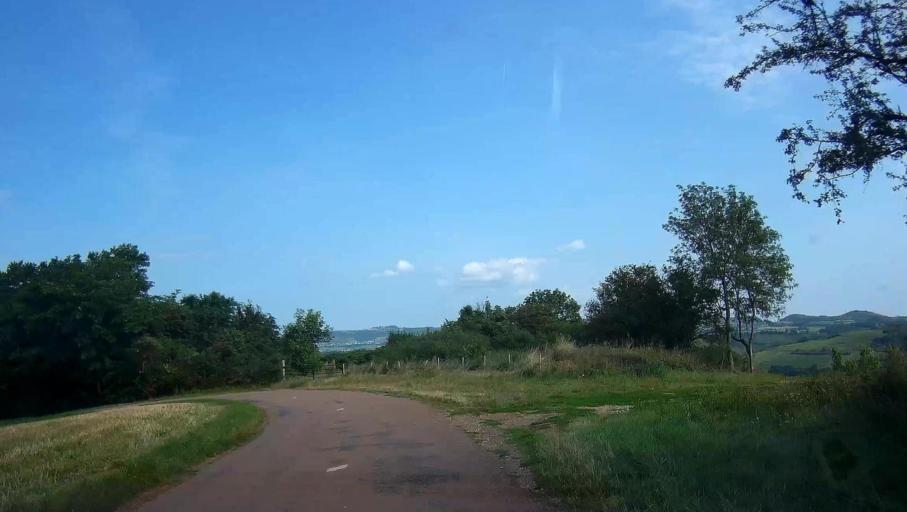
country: FR
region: Bourgogne
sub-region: Departement de la Cote-d'Or
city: Nolay
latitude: 46.9060
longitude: 4.6294
